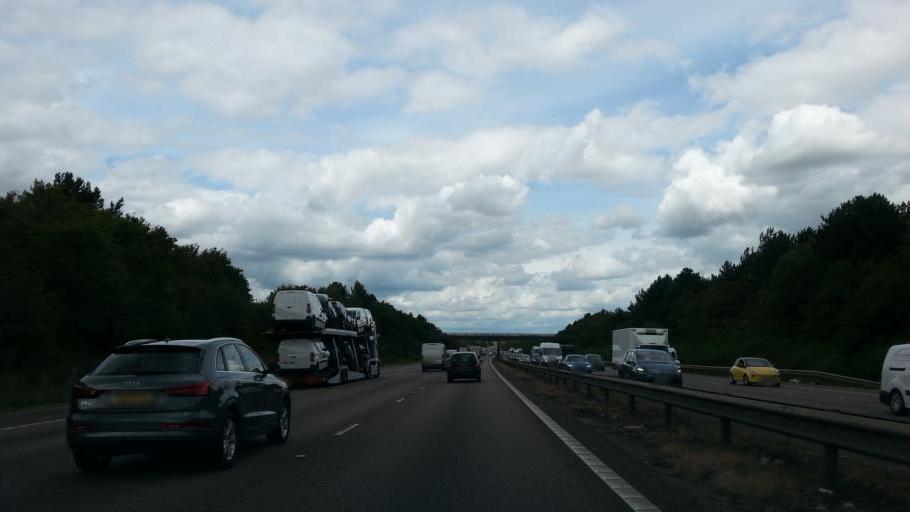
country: GB
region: England
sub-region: Essex
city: Epping
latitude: 51.7211
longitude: 0.1421
